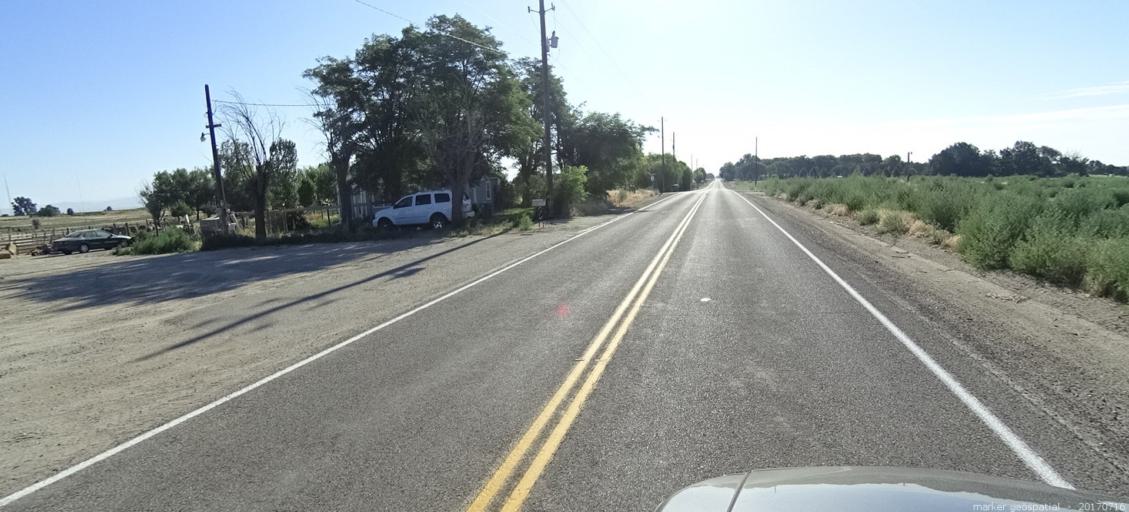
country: US
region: Idaho
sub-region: Ada County
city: Kuna
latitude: 43.5465
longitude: -116.4079
